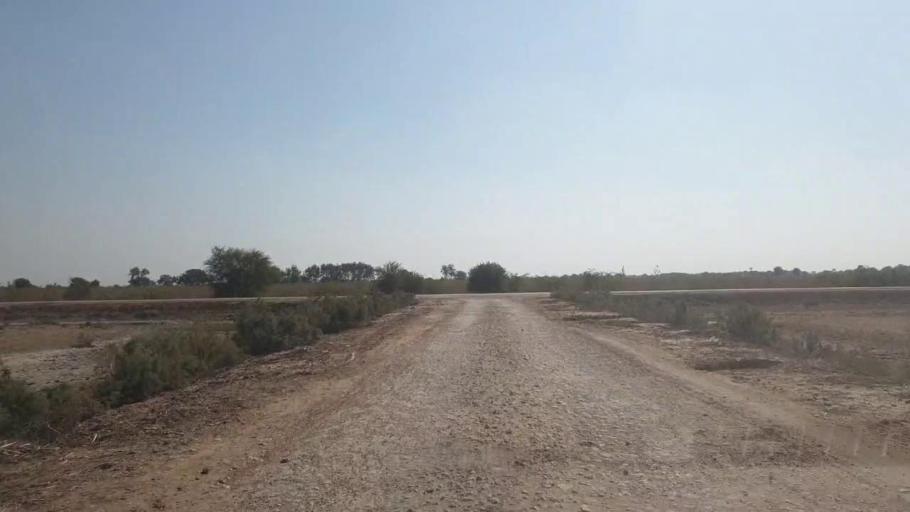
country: PK
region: Sindh
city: Chambar
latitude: 25.2950
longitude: 68.7418
